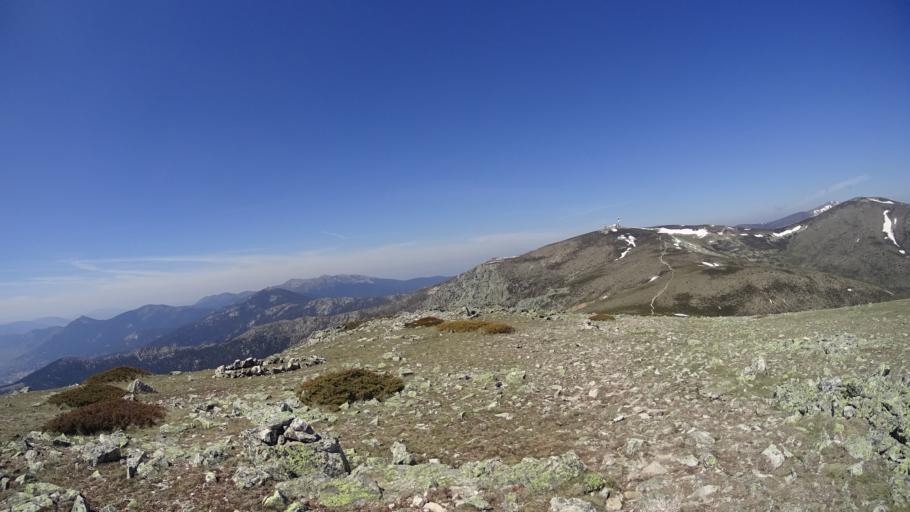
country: ES
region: Madrid
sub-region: Provincia de Madrid
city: Becerril de la Sierra
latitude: 40.7678
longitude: -3.9689
